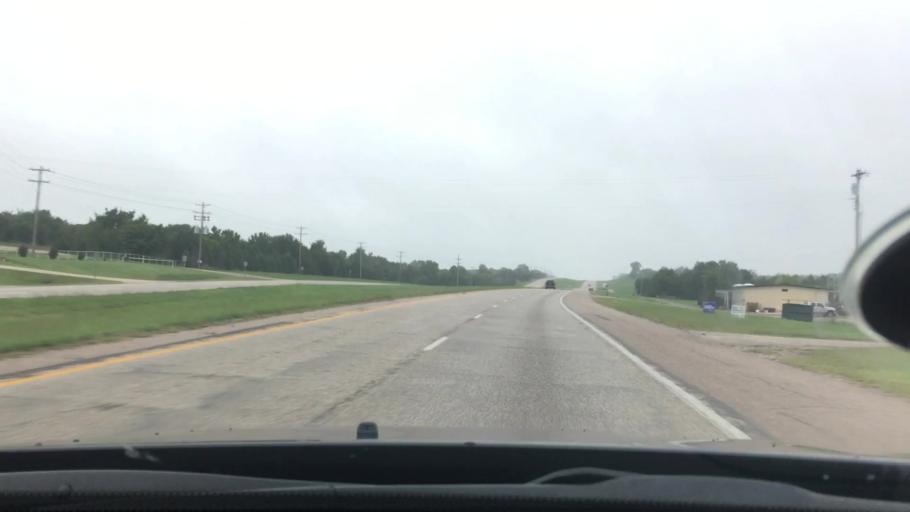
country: US
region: Oklahoma
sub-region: Seminole County
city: Seminole
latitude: 35.2778
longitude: -96.6706
